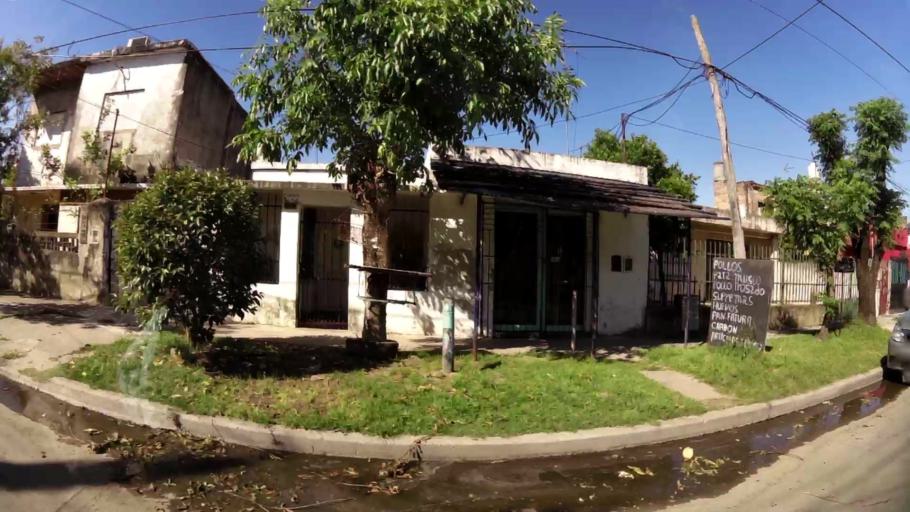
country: AR
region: Buenos Aires
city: Caseros
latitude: -34.5455
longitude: -58.5899
